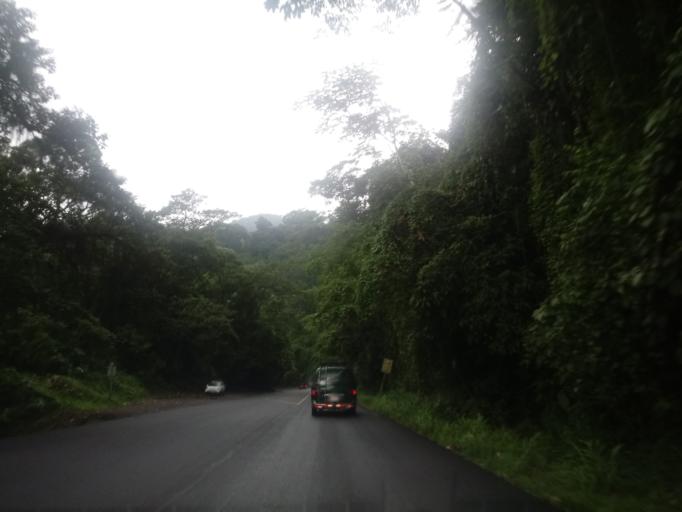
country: CR
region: San Jose
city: Dulce Nombre de Jesus
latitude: 10.1492
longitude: -83.9567
